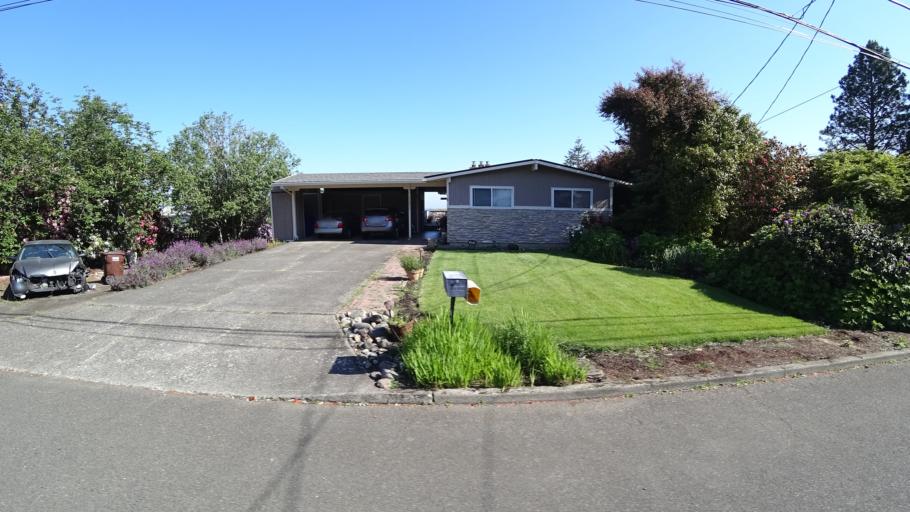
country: US
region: Oregon
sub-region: Multnomah County
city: Lents
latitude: 45.4660
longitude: -122.5466
